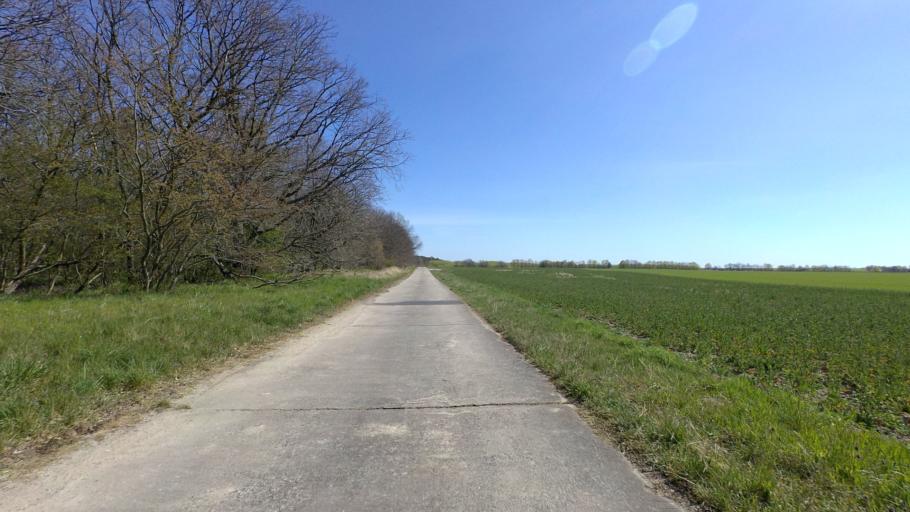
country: DE
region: Brandenburg
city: Mittenwalde
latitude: 52.3171
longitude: 13.5296
